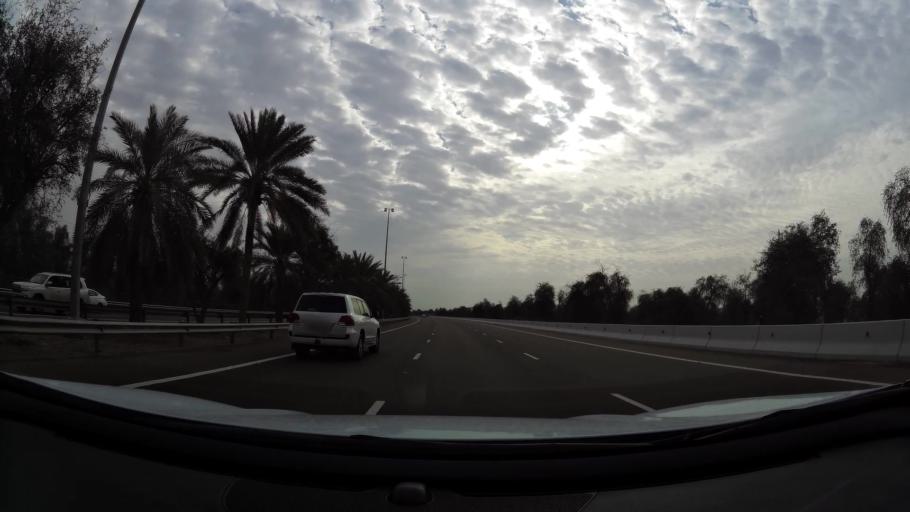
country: AE
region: Abu Dhabi
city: Al Ain
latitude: 24.1701
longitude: 55.2430
